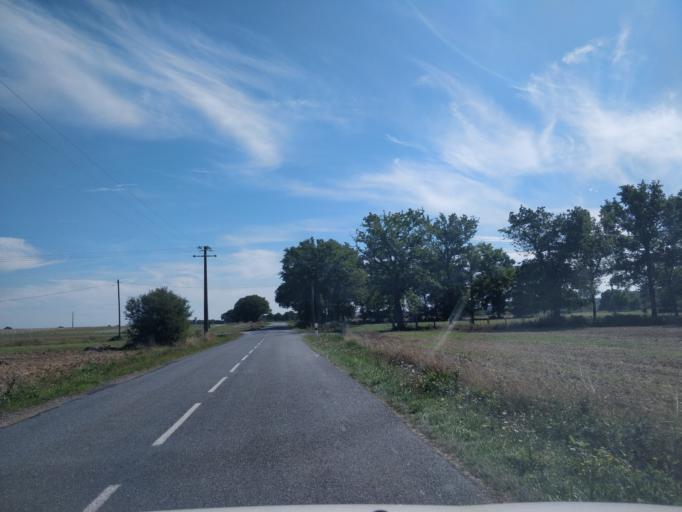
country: FR
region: Brittany
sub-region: Departement d'Ille-et-Vilaine
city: Grand-Fougeray
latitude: 47.6886
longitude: -1.7214
